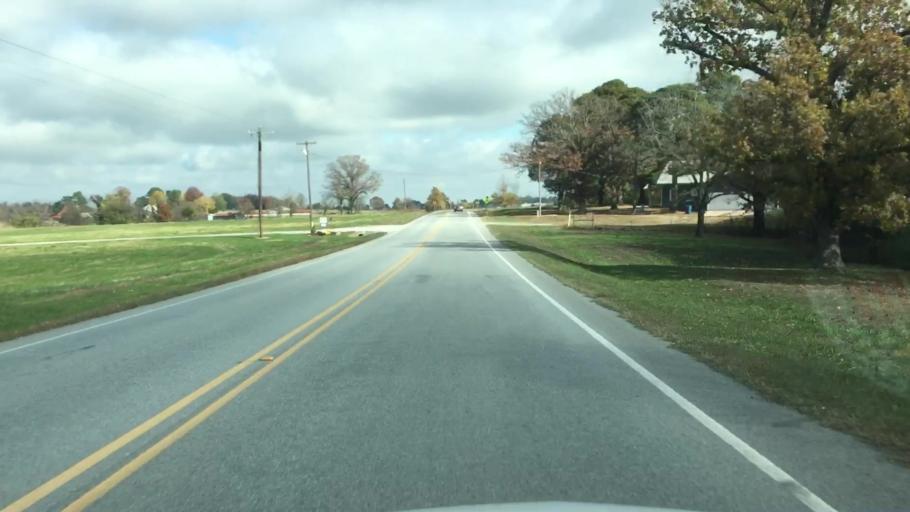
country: US
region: Arkansas
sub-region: Benton County
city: Gentry
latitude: 36.2603
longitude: -94.3705
